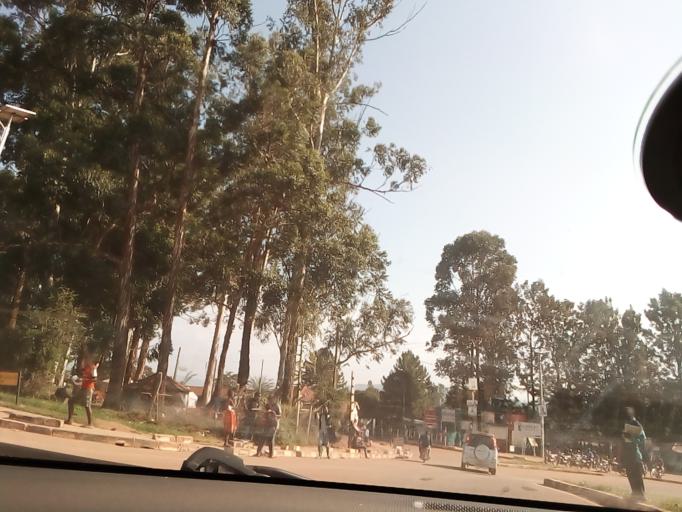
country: UG
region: Central Region
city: Masaka
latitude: -0.3303
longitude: 31.7377
